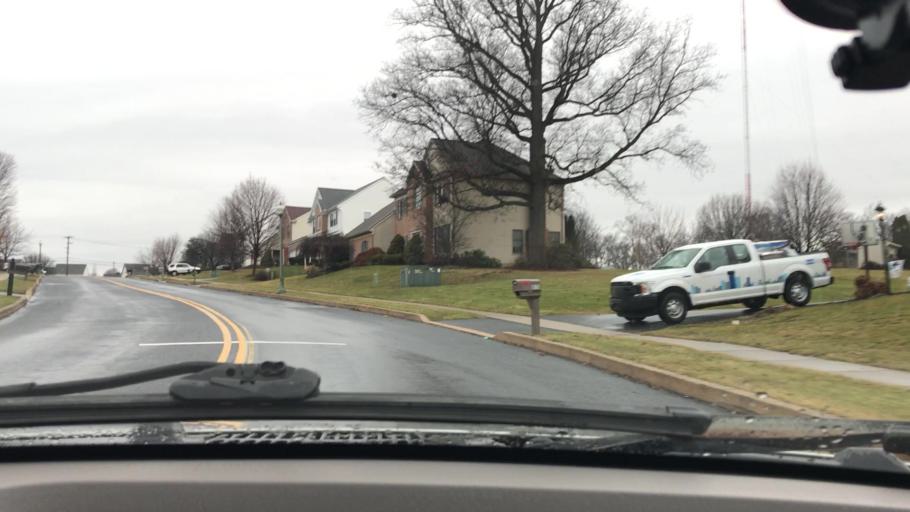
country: US
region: Pennsylvania
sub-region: Lancaster County
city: Elizabethtown
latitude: 40.1699
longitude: -76.5952
